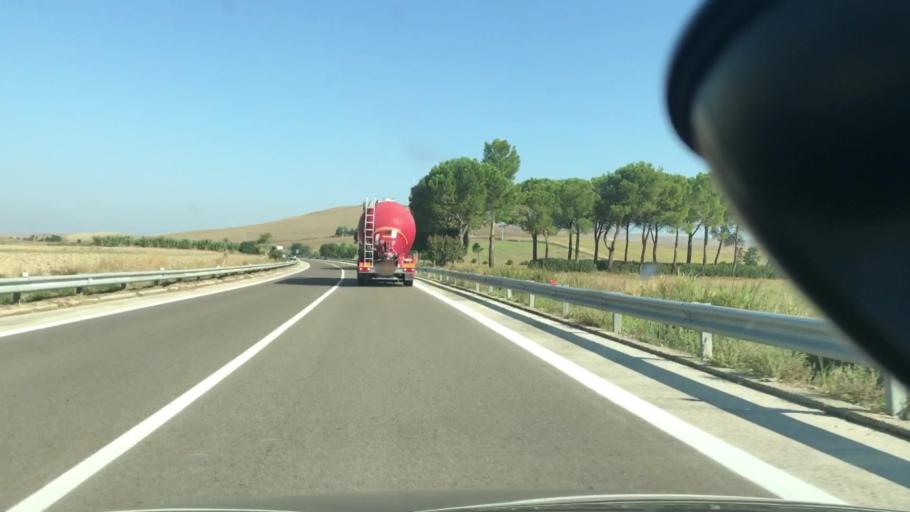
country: IT
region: Basilicate
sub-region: Provincia di Matera
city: Irsina
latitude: 40.8061
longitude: 16.2730
